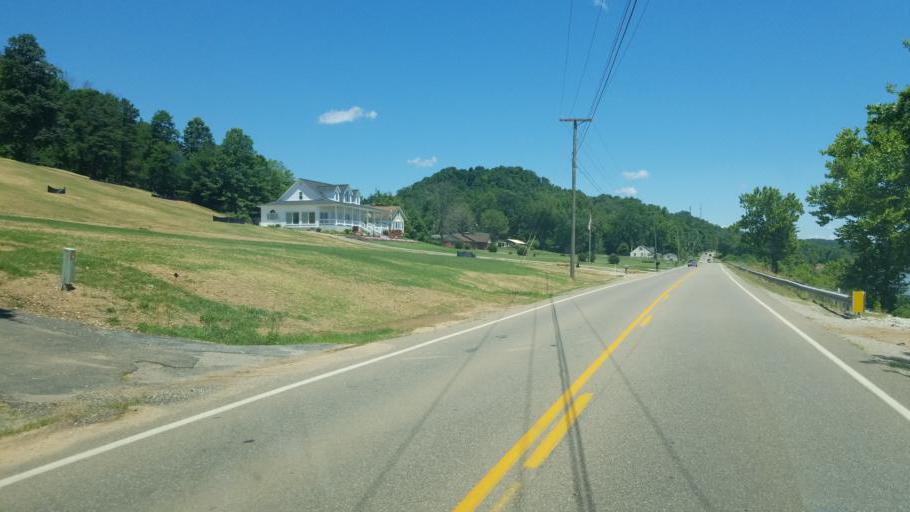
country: US
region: Ohio
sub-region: Gallia County
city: Gallipolis
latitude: 38.7853
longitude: -82.2227
